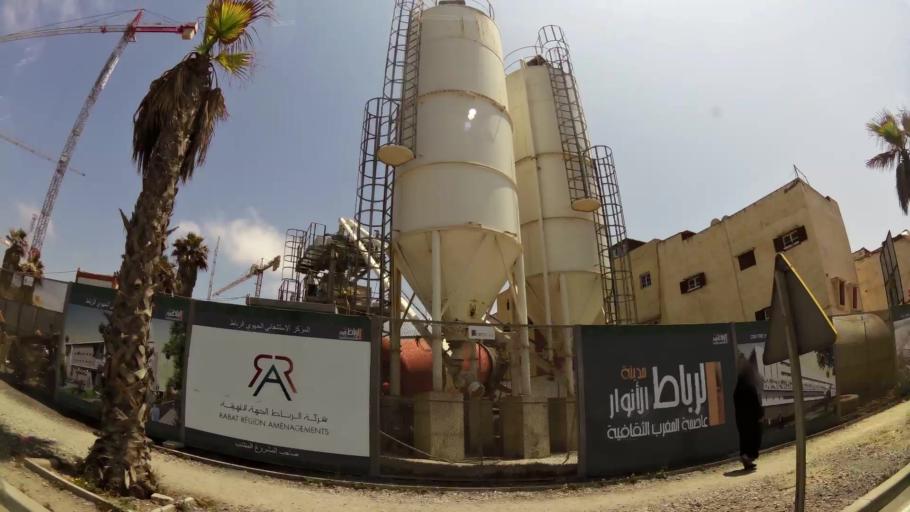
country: MA
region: Rabat-Sale-Zemmour-Zaer
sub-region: Rabat
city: Rabat
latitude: 34.0120
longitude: -6.8642
